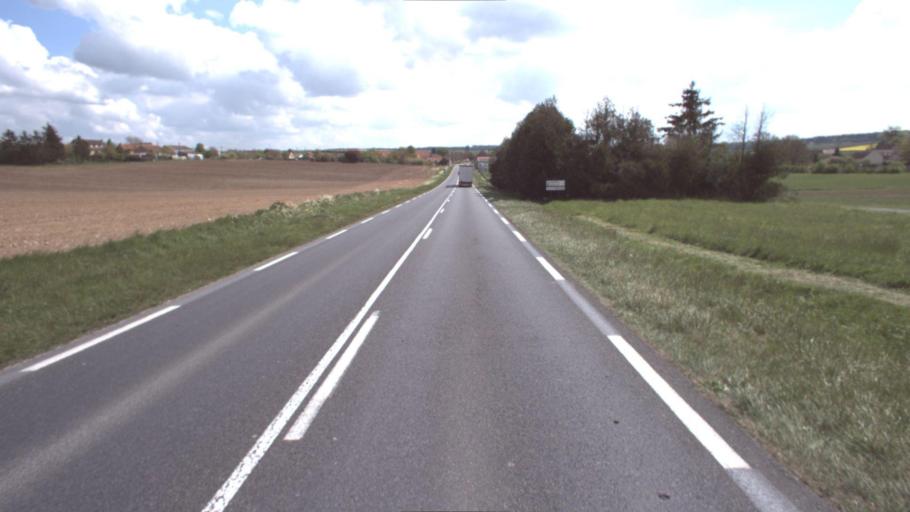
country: FR
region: Ile-de-France
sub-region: Departement de Seine-et-Marne
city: La Ferte-Gaucher
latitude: 48.6971
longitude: 3.2861
